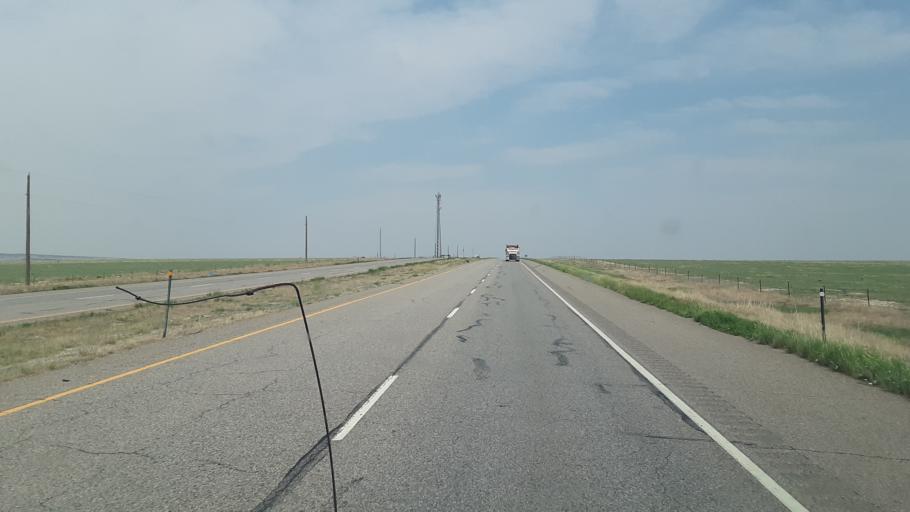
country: US
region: Colorado
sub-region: Fremont County
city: Penrose
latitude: 38.3616
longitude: -104.8799
